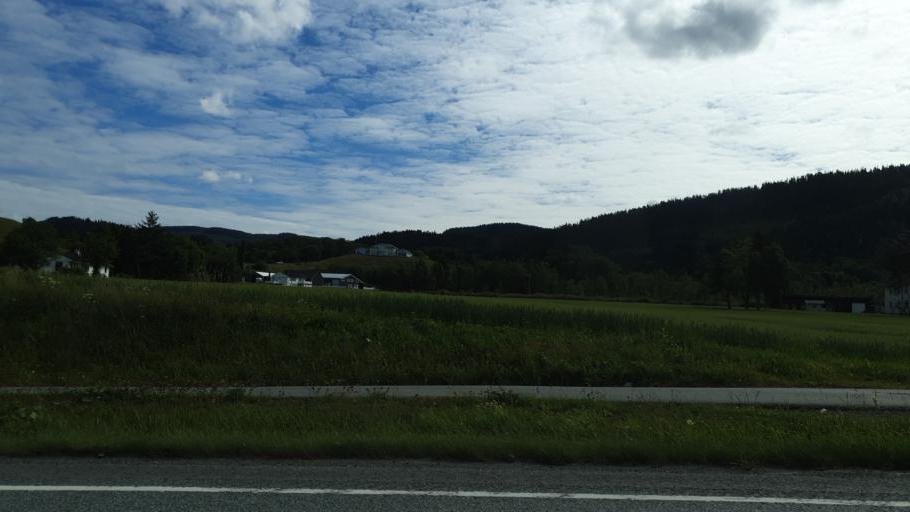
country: NO
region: Sor-Trondelag
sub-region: Melhus
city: Lundamo
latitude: 63.1749
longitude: 10.3167
